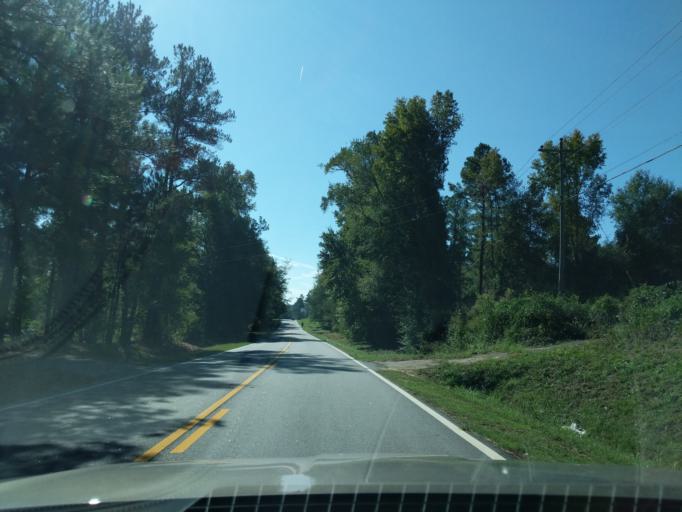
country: US
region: Georgia
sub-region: Richmond County
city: Hephzibah
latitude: 33.3144
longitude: -82.0190
